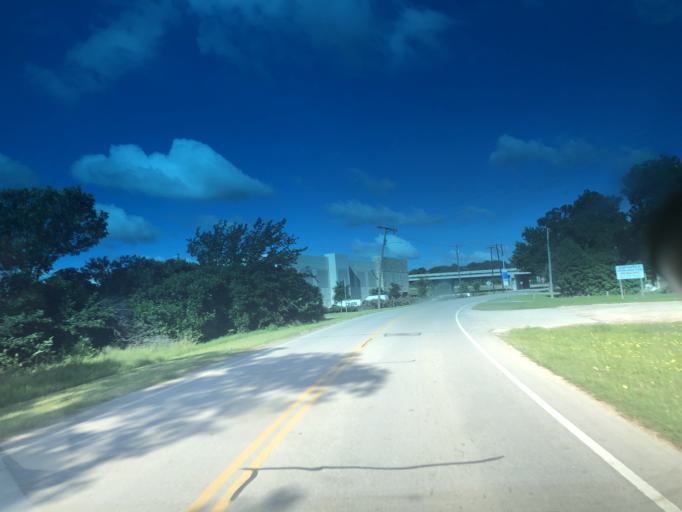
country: US
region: Texas
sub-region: Dallas County
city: Grand Prairie
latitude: 32.8036
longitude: -97.0156
